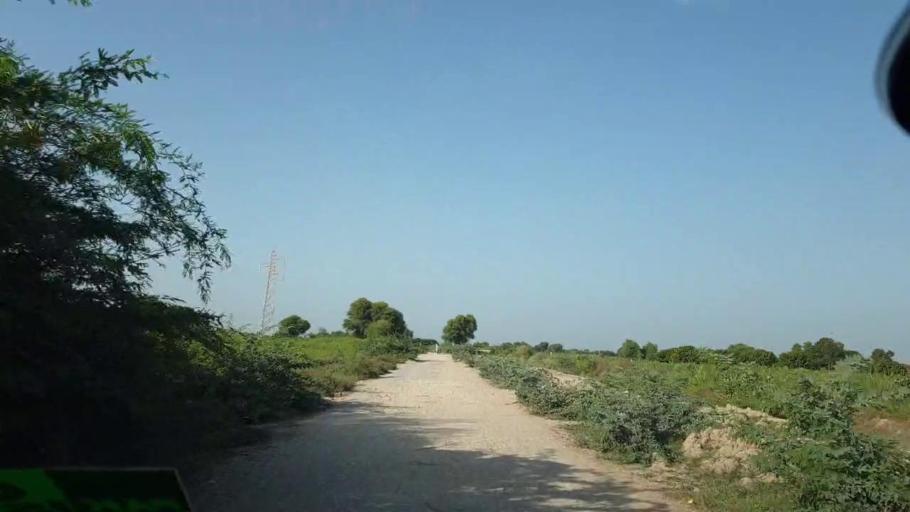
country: PK
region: Sindh
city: Naukot
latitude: 24.7391
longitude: 69.2199
